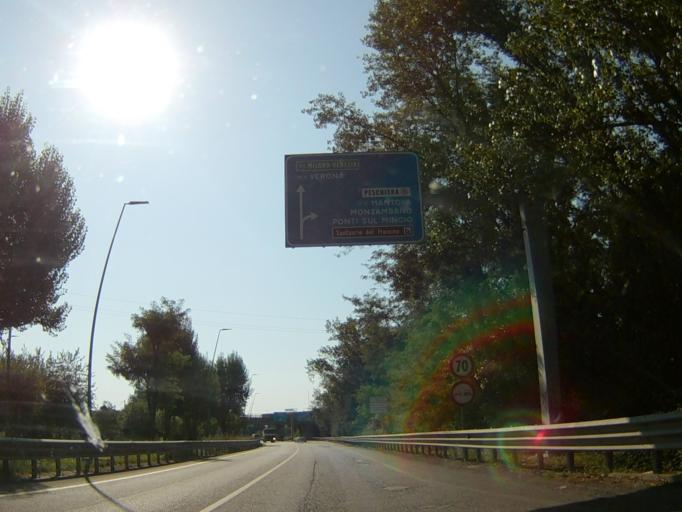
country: IT
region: Veneto
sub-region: Provincia di Verona
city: Peschiera del Garda
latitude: 45.4325
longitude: 10.6838
